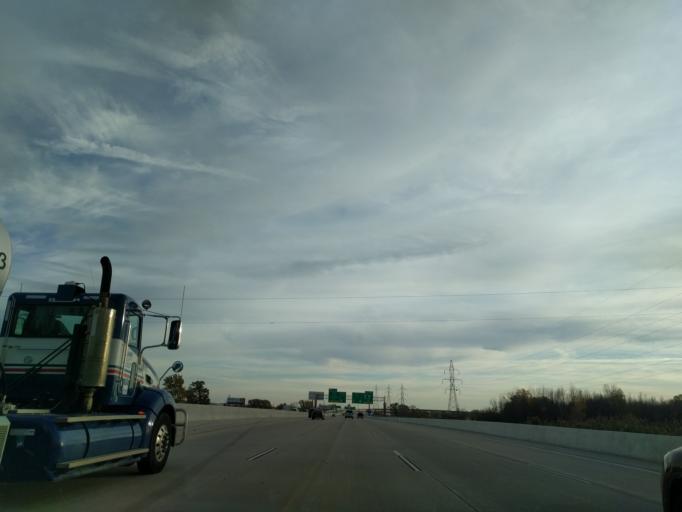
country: US
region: Wisconsin
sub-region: Brown County
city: Howard
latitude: 44.5759
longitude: -88.0487
